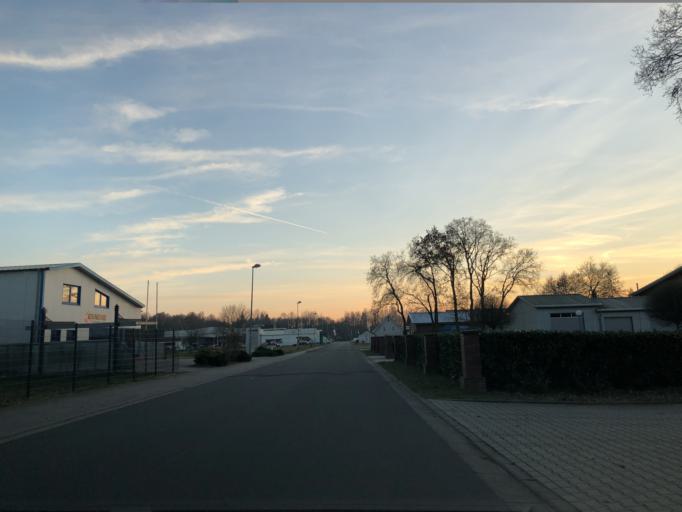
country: DE
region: Lower Saxony
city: Papenburg
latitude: 53.0943
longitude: 7.4054
